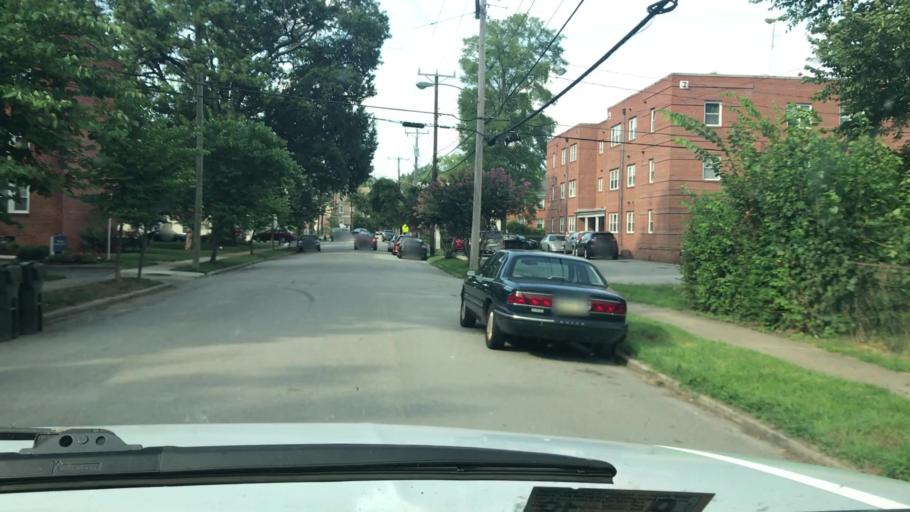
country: US
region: Virginia
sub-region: City of Richmond
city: Richmond
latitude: 37.5612
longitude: -77.4833
